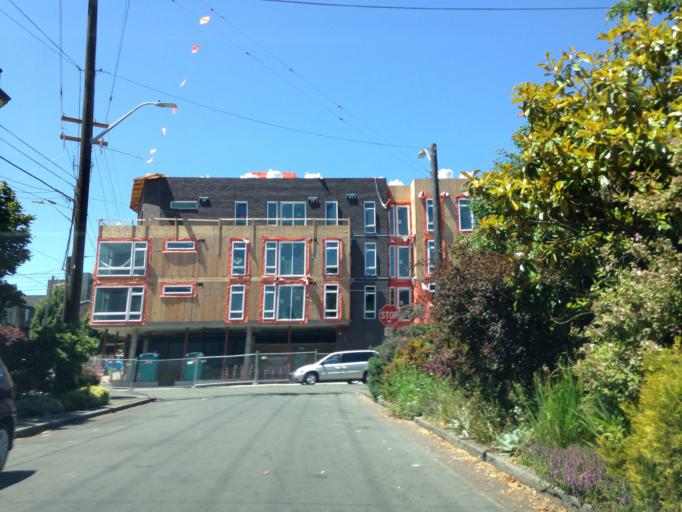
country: US
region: Washington
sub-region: King County
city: Seattle
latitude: 47.6245
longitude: -122.3122
